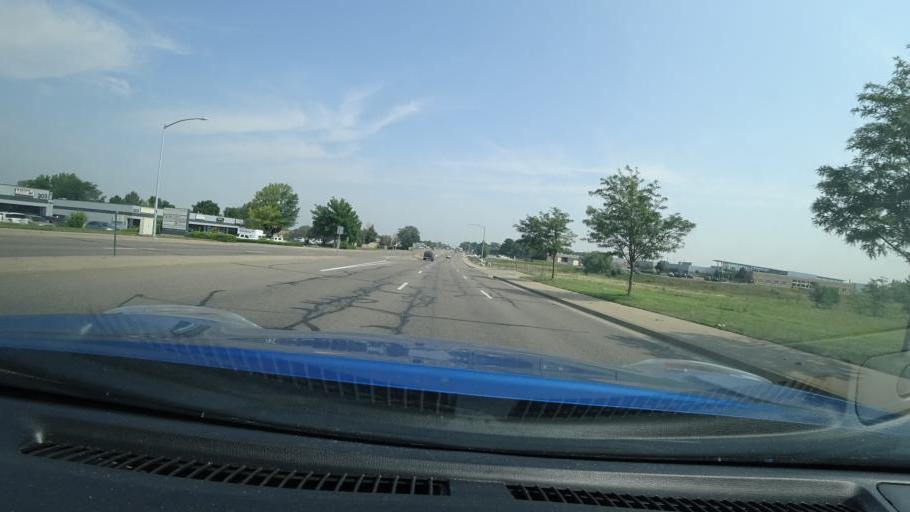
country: US
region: Colorado
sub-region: Adams County
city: Aurora
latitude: 39.7201
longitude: -104.7909
